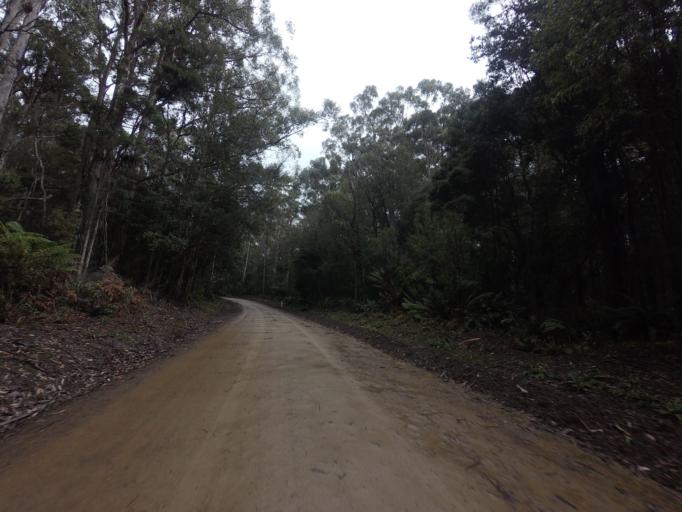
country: AU
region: Tasmania
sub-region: Huon Valley
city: Geeveston
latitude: -43.5566
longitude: 146.8899
